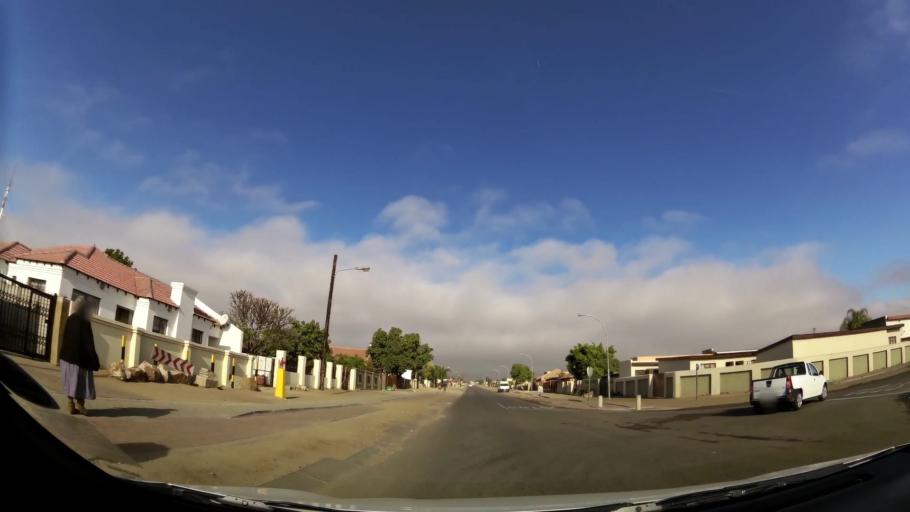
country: ZA
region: Limpopo
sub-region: Capricorn District Municipality
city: Polokwane
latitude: -23.8444
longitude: 29.3895
